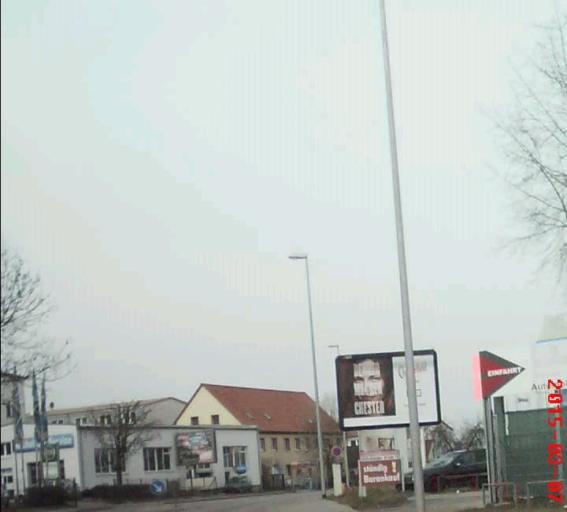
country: DE
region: Thuringia
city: Erfurt
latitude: 51.0099
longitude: 11.0170
